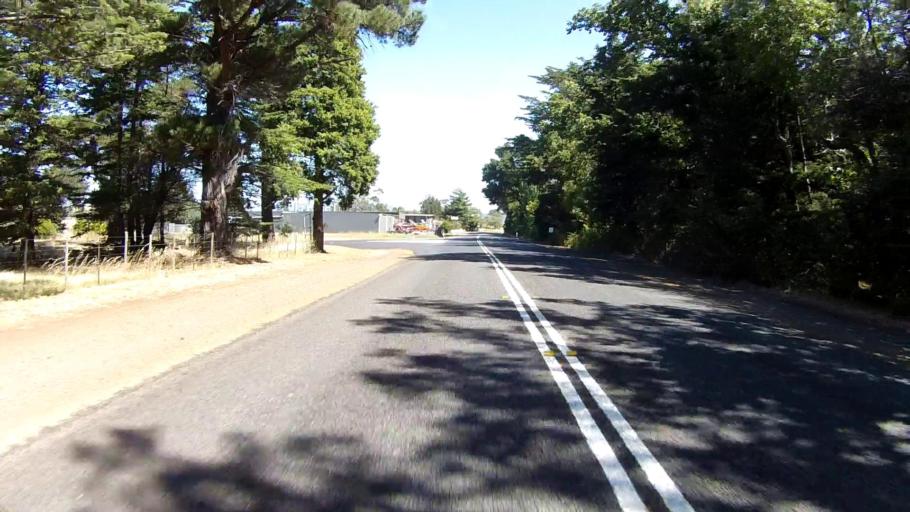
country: AU
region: Tasmania
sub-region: Sorell
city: Sorell
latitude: -42.4977
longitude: 147.9225
